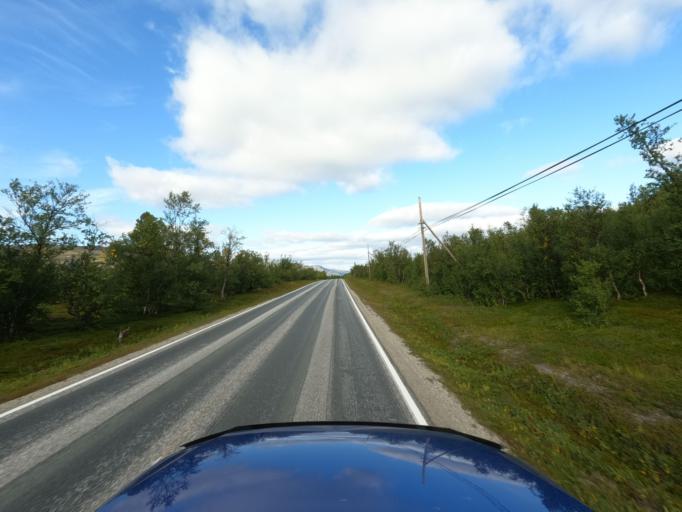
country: NO
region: Finnmark Fylke
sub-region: Porsanger
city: Lakselv
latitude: 69.9925
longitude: 24.9508
